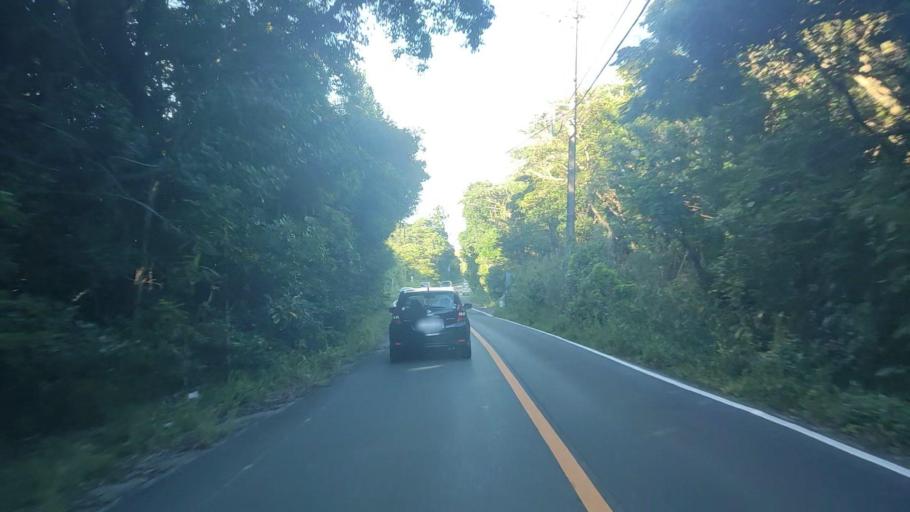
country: JP
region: Mie
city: Toba
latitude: 34.3321
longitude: 136.8619
